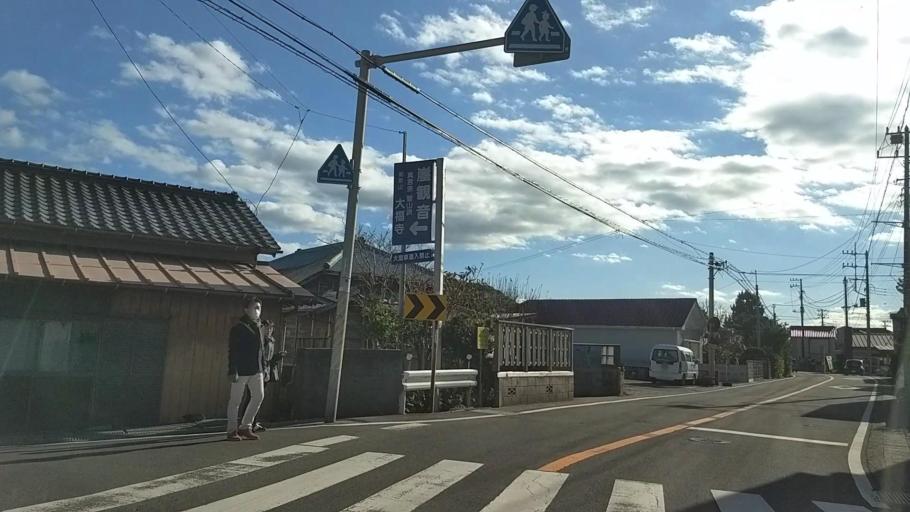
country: JP
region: Chiba
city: Tateyama
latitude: 35.0290
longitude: 139.8422
